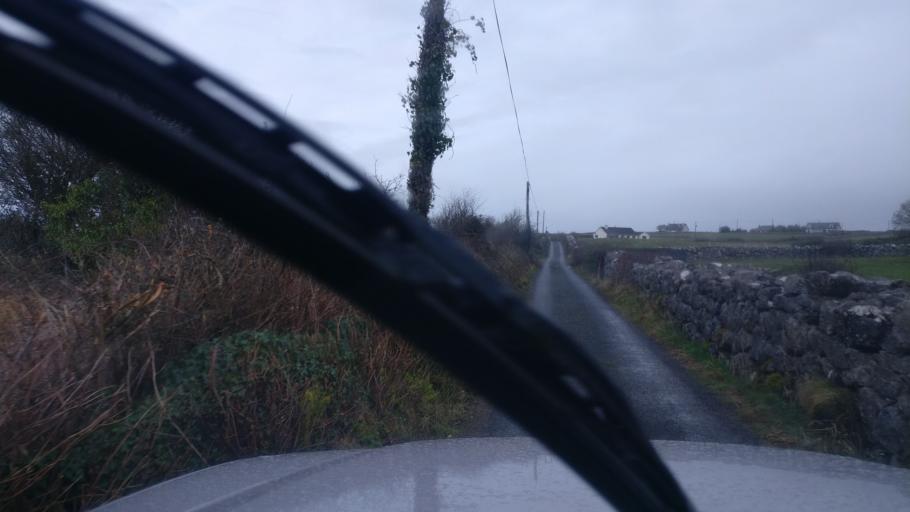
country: IE
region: Connaught
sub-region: County Galway
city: Loughrea
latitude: 53.1943
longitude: -8.6815
